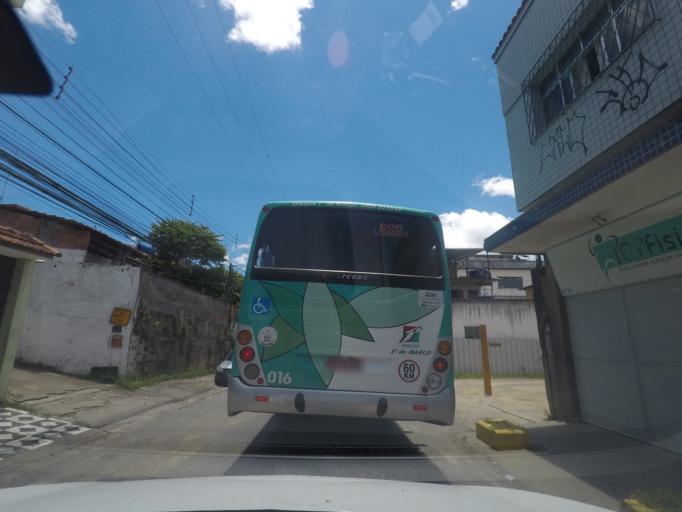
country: BR
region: Rio de Janeiro
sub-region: Teresopolis
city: Teresopolis
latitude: -22.4304
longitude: -42.9657
